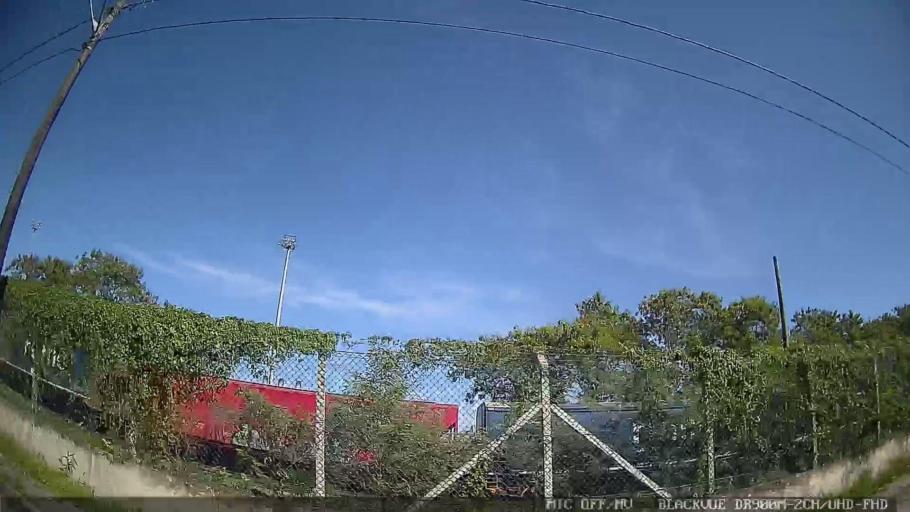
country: BR
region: Sao Paulo
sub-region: Santos
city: Santos
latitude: -23.9577
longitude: -46.2889
